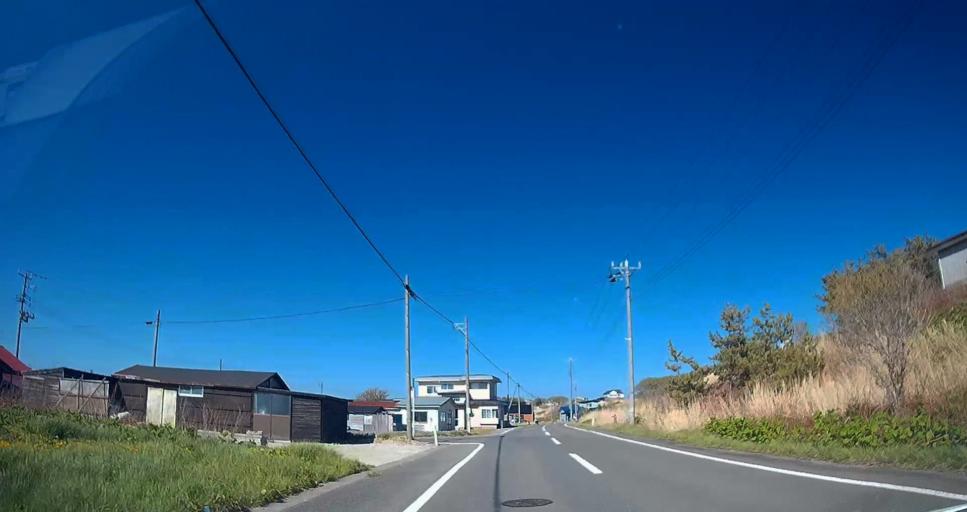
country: JP
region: Hokkaido
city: Hakodate
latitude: 41.5397
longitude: 140.9108
